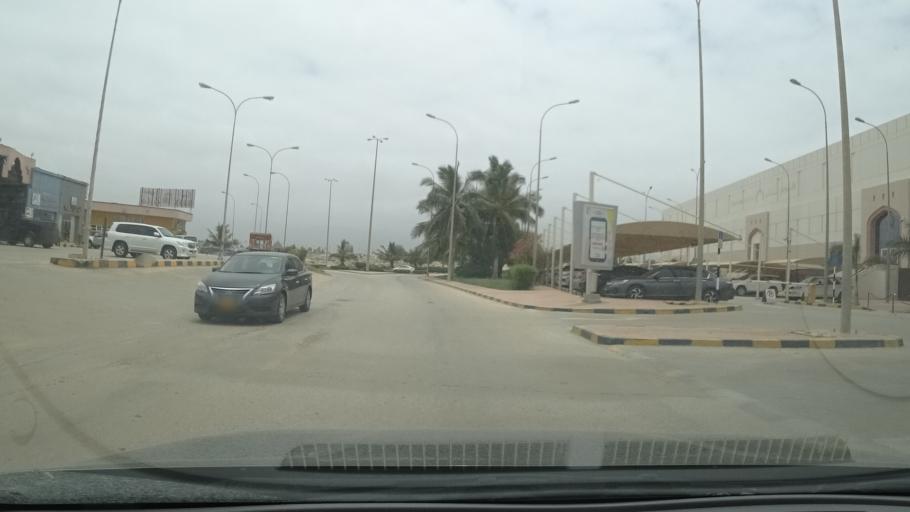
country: OM
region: Zufar
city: Salalah
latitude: 17.0225
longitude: 54.0646
